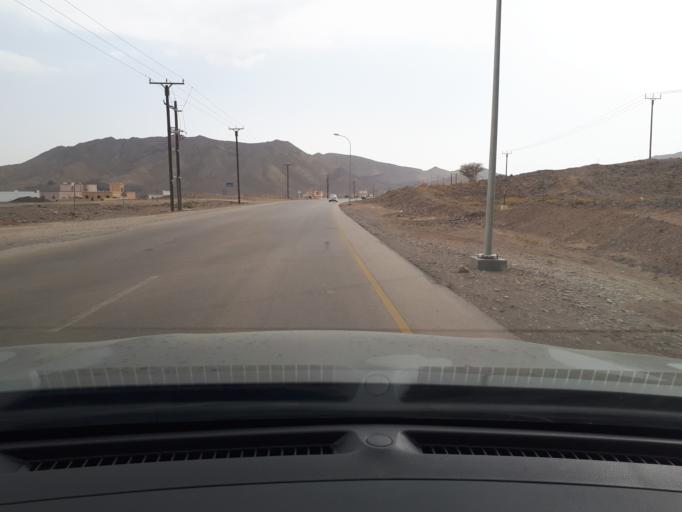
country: OM
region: Ash Sharqiyah
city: Badiyah
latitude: 22.5419
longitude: 58.9886
